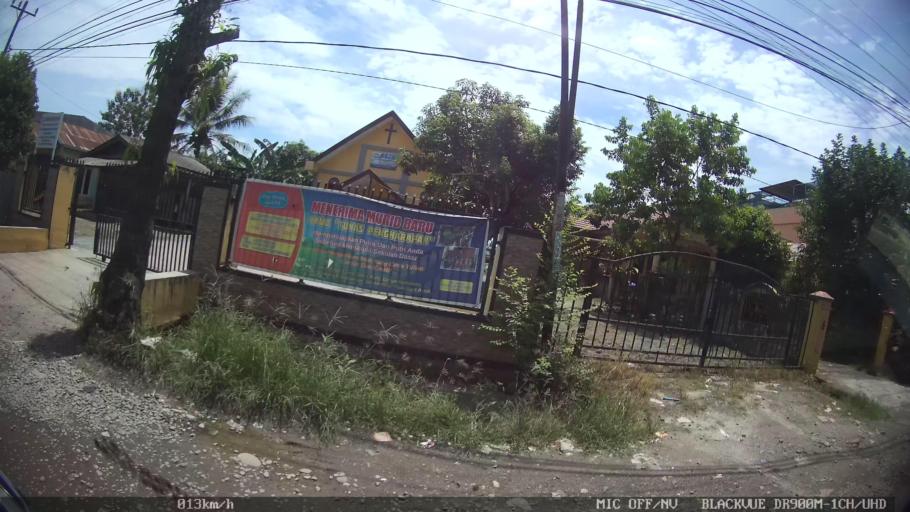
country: ID
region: North Sumatra
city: Perbaungan
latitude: 3.5406
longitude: 98.8825
